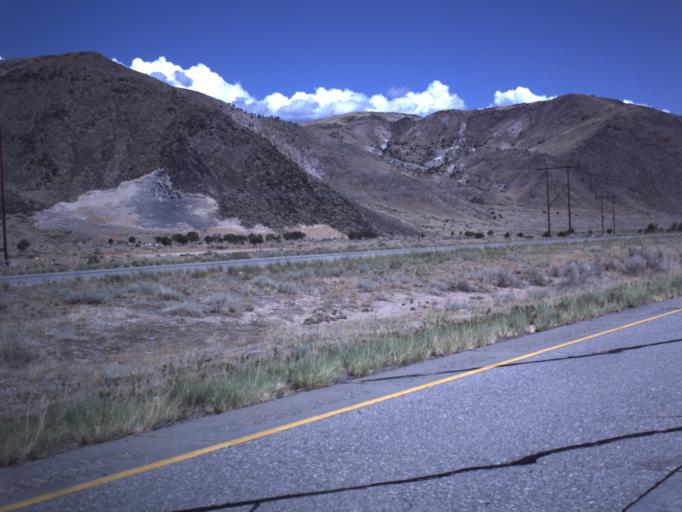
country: US
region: Utah
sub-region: Sevier County
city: Richfield
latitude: 38.7114
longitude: -112.1367
